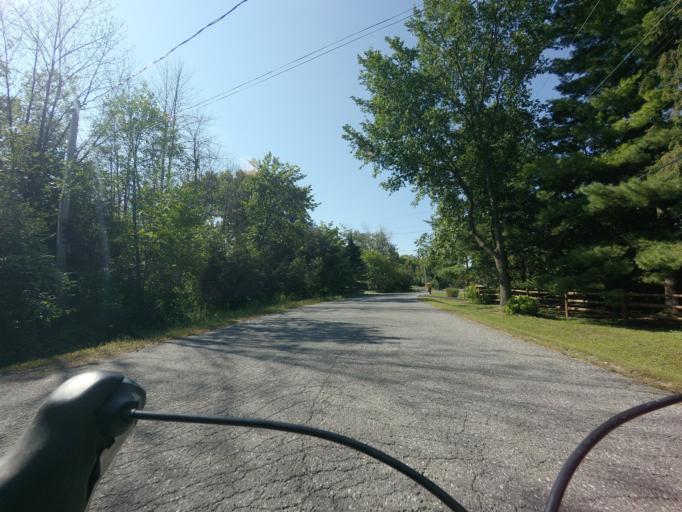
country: CA
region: Ontario
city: Bells Corners
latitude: 45.4605
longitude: -75.9692
